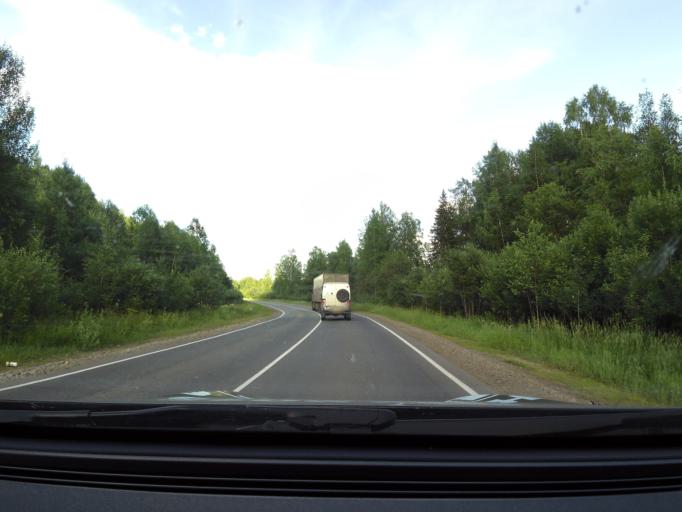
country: RU
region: Kirov
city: Belorechensk
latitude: 58.7072
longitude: 52.2643
